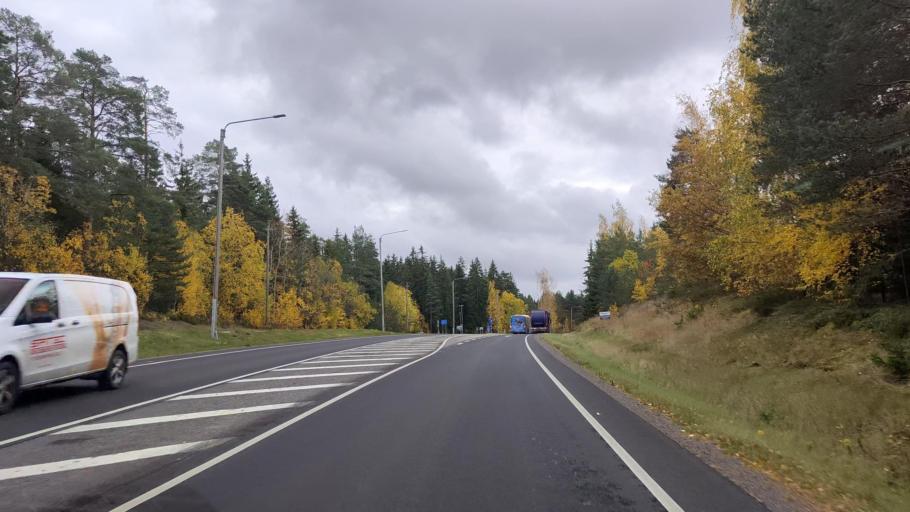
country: FI
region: Varsinais-Suomi
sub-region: Turku
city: Kaarina
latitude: 60.4594
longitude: 22.3640
